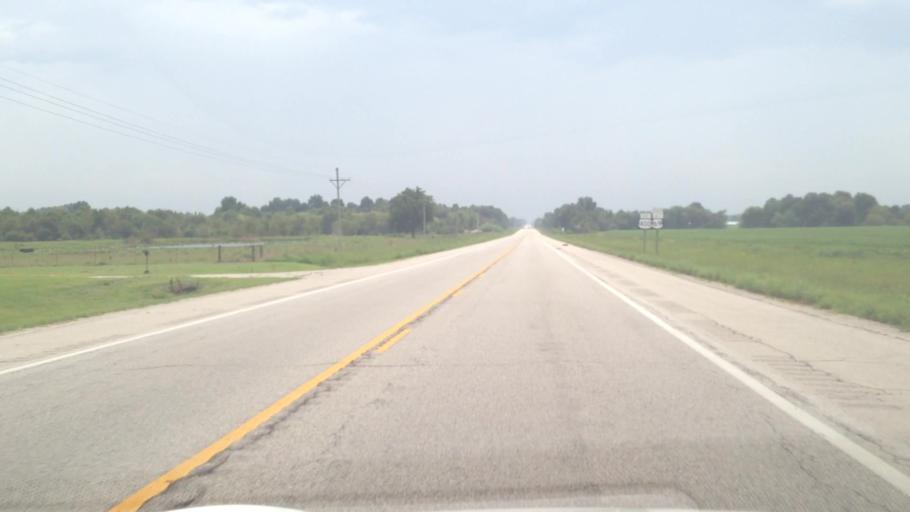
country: US
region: Kansas
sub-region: Cherokee County
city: Galena
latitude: 37.1469
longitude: -94.7044
